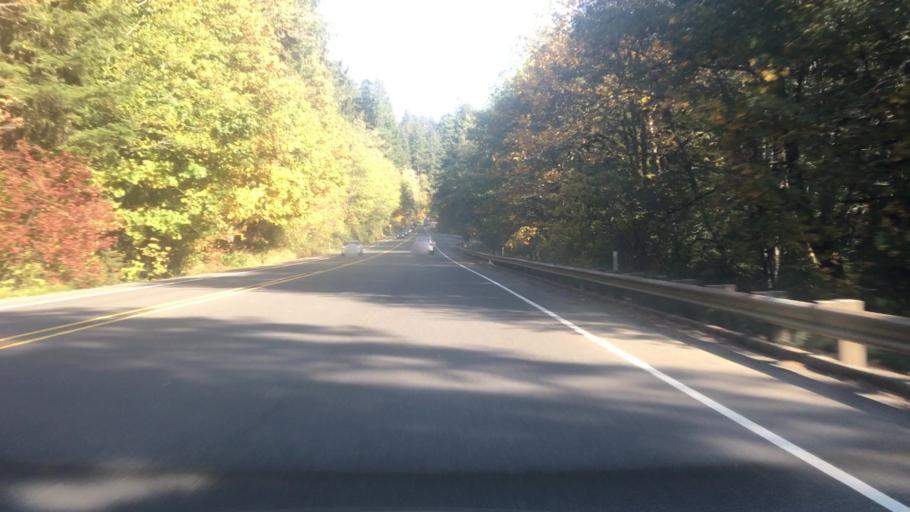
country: US
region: Oregon
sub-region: Lincoln County
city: Rose Lodge
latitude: 45.0503
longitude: -123.7826
